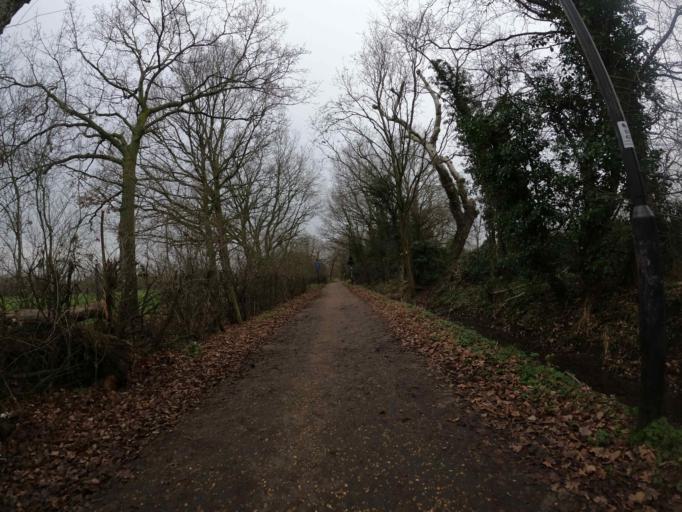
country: GB
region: England
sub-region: Greater London
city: Greenford
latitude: 51.5169
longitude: -0.3450
